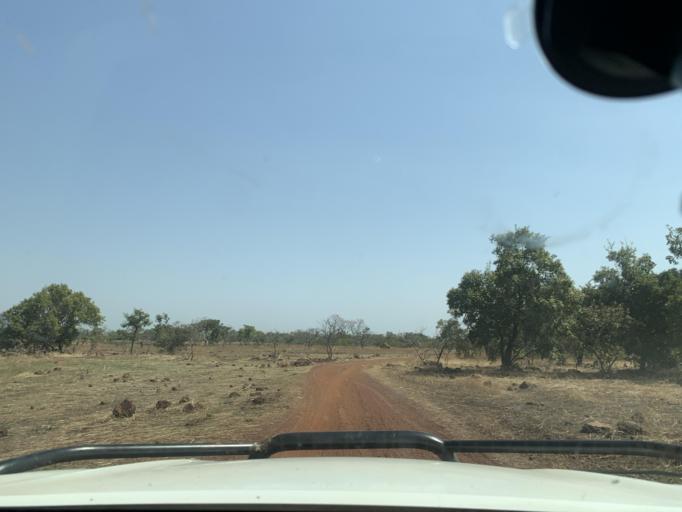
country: ML
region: Sikasso
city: Kolondieba
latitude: 10.8343
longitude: -6.7872
